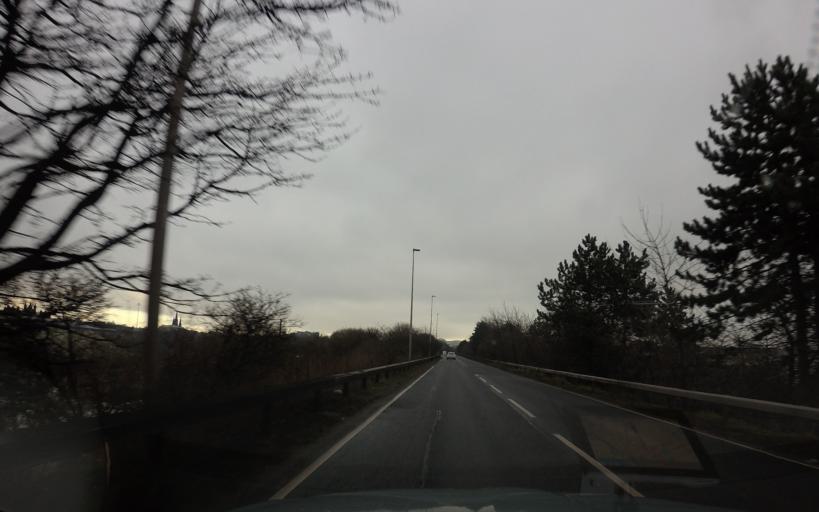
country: GB
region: Scotland
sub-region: Edinburgh
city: Edinburgh
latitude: 55.9411
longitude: -3.2343
